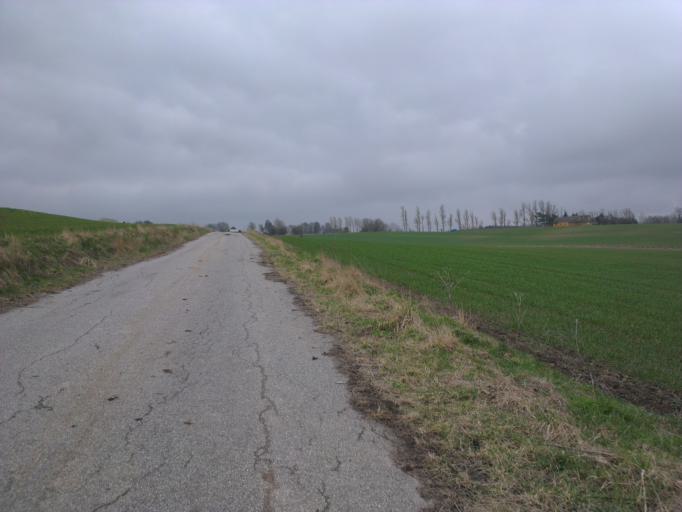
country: DK
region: Capital Region
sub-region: Frederikssund Kommune
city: Frederikssund
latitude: 55.8756
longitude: 12.0774
